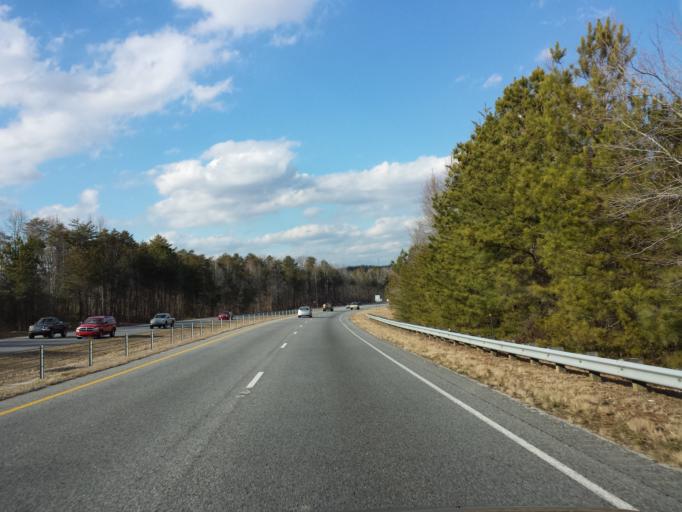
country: US
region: Georgia
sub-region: Lumpkin County
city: Dahlonega
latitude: 34.4333
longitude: -83.9933
